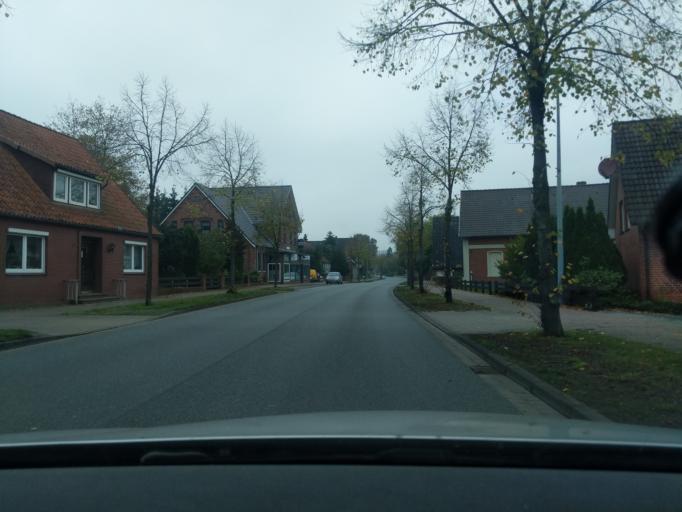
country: DE
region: Lower Saxony
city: Hemmoor
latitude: 53.6934
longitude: 9.1521
